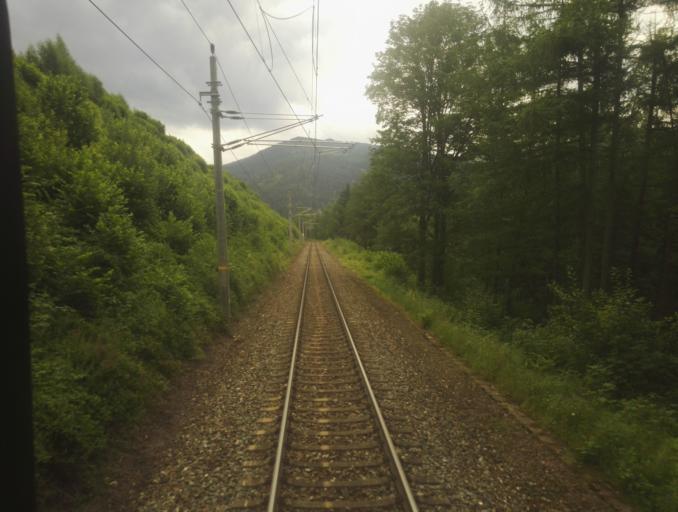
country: AT
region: Salzburg
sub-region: Politischer Bezirk Sankt Johann im Pongau
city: Eben im Pongau
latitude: 47.4199
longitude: 13.3767
